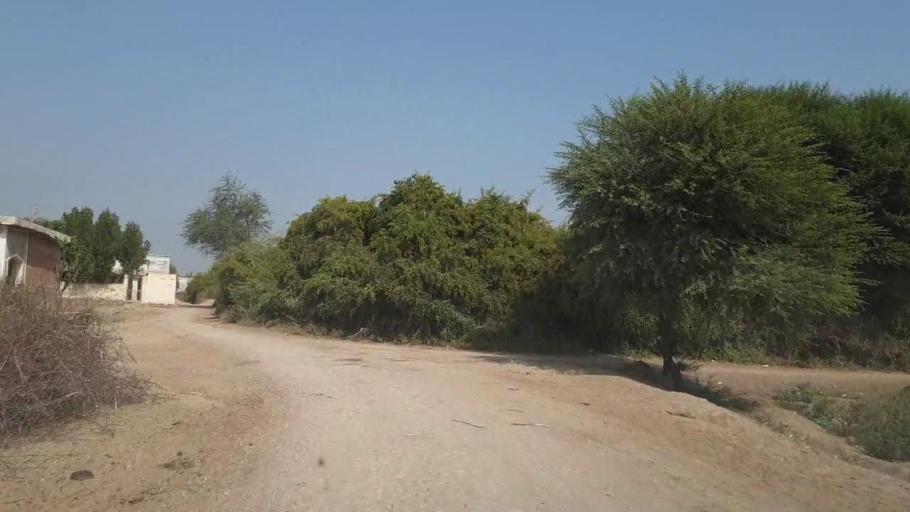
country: PK
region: Sindh
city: Mirpur Khas
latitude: 25.6539
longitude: 69.1063
